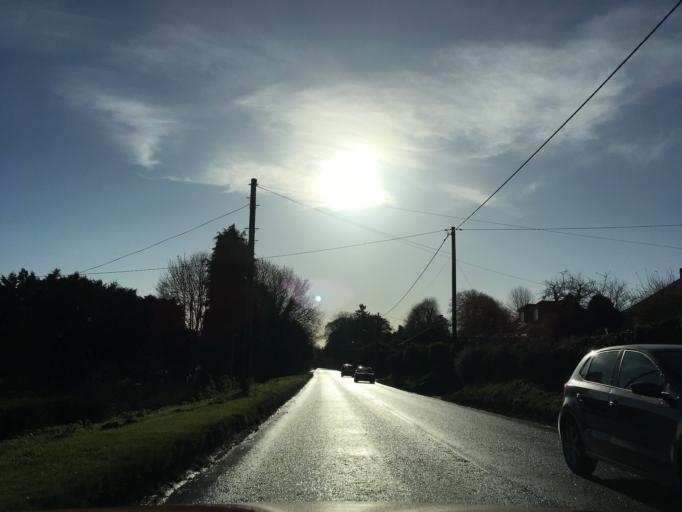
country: GB
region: England
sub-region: Wiltshire
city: Collingbourne Kingston
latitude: 51.2891
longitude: -1.6533
